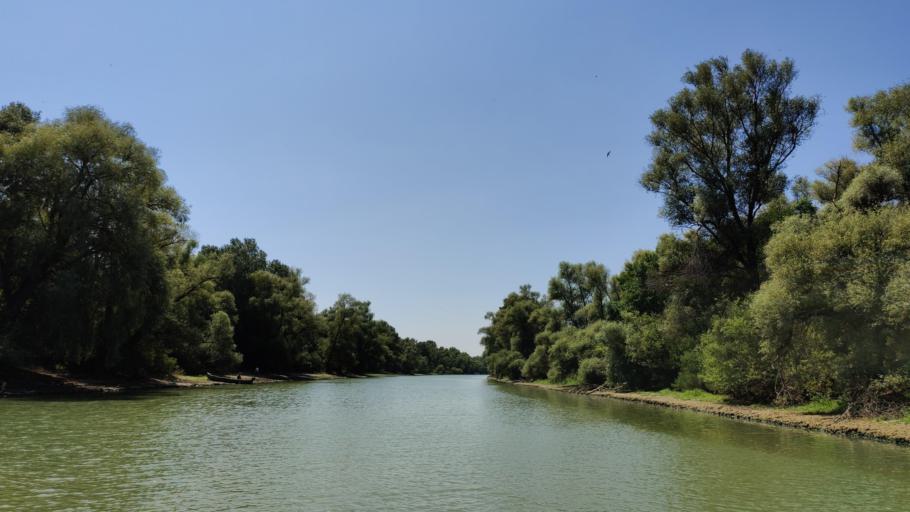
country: RO
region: Tulcea
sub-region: Comuna Nufaru
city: Nufaru
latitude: 45.2266
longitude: 28.8878
